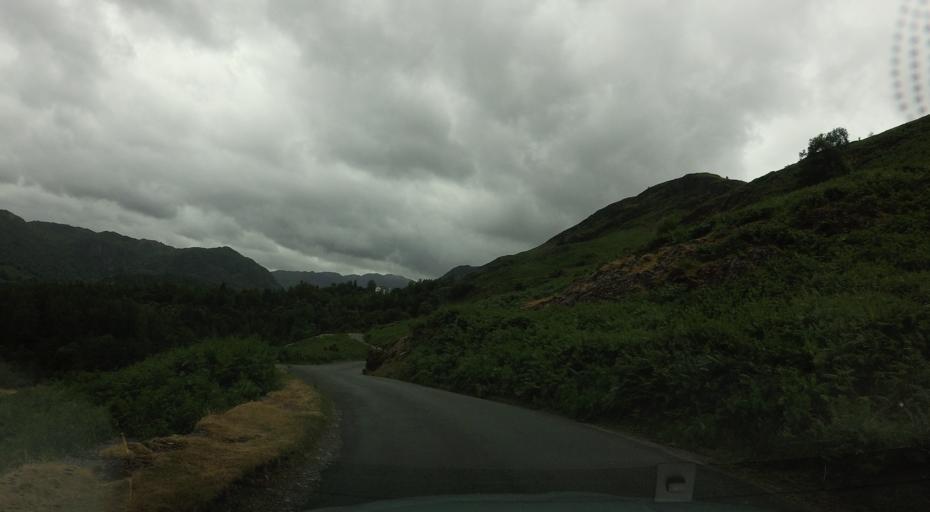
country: GB
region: England
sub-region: Cumbria
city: Keswick
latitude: 54.5664
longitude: -3.1626
